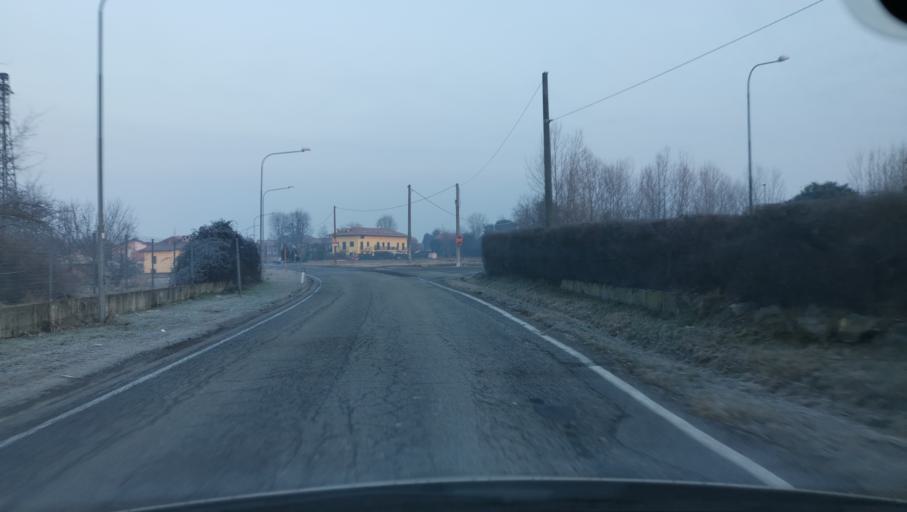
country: IT
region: Piedmont
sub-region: Provincia di Torino
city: San Benigno Canavese
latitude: 45.2188
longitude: 7.7923
